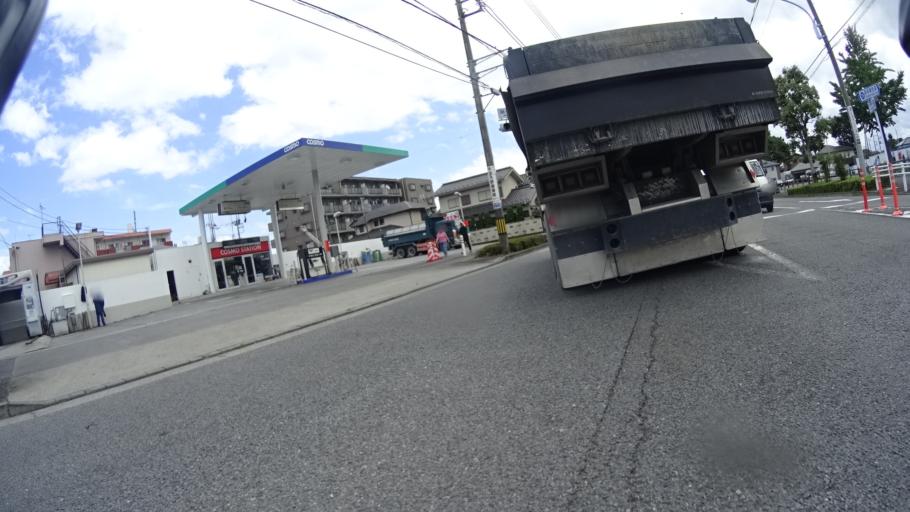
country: JP
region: Tokyo
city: Fussa
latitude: 35.7279
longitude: 139.3347
